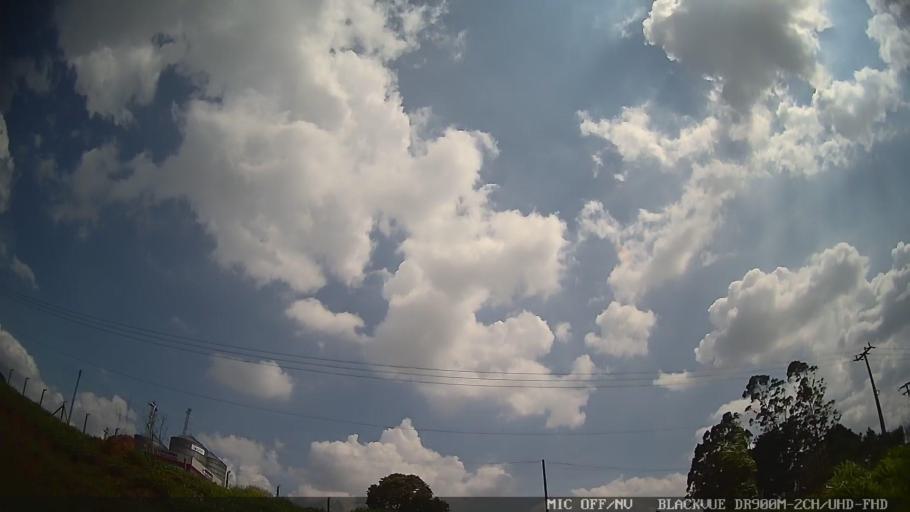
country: BR
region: Sao Paulo
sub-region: Braganca Paulista
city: Braganca Paulista
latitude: -22.9447
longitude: -46.6669
